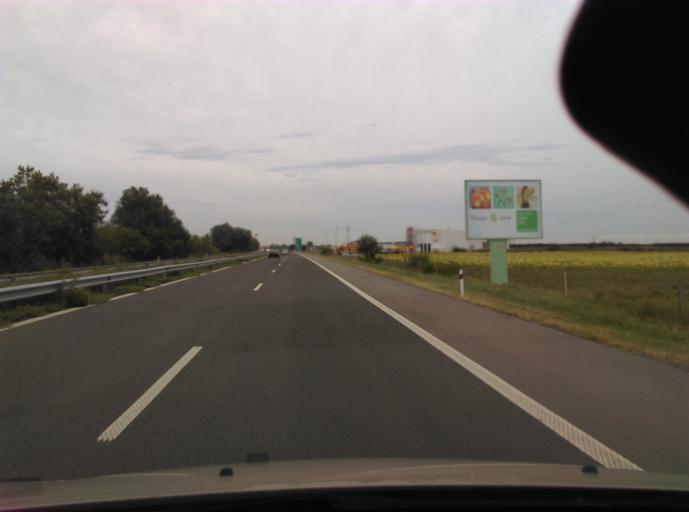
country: BG
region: Plovdiv
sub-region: Obshtina Plovdiv
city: Plovdiv
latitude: 42.2106
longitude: 24.7966
